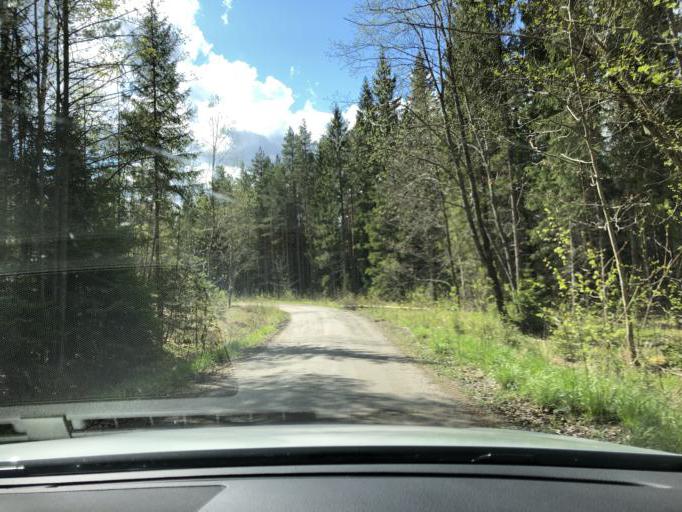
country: SE
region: Uppsala
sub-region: Heby Kommun
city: Tarnsjo
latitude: 60.2637
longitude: 16.9142
